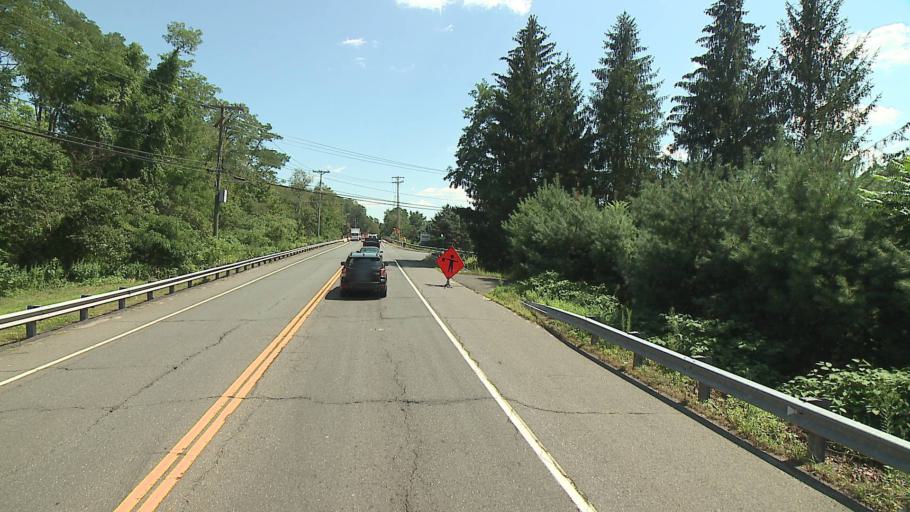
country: US
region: Connecticut
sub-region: Hartford County
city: Collinsville
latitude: 41.7654
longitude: -72.8981
